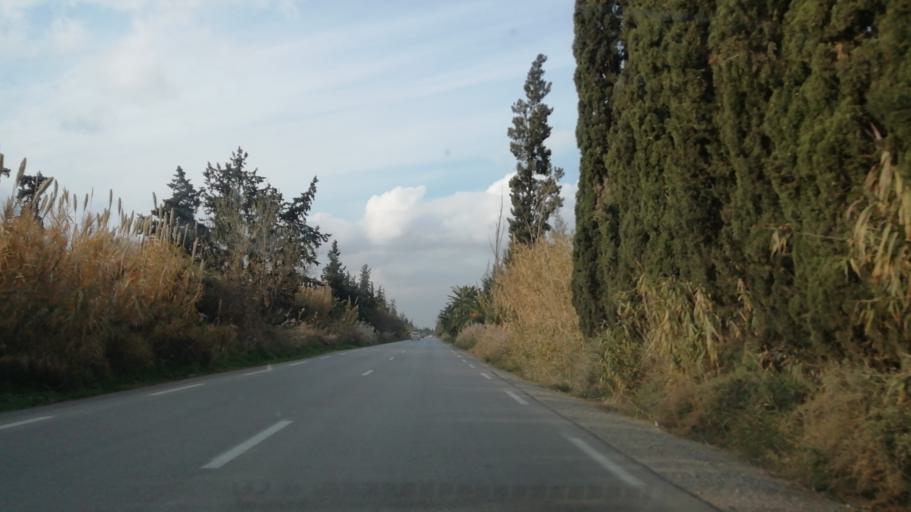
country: DZ
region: Mascara
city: Mascara
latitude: 35.6216
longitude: 0.0458
